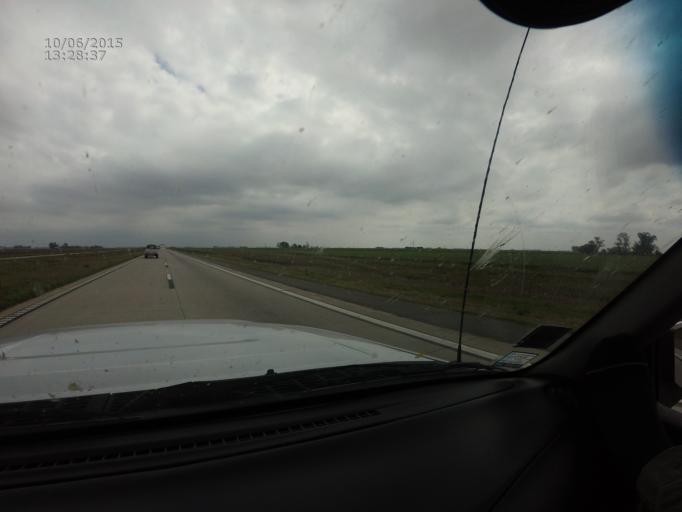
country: AR
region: Cordoba
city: Leones
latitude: -32.6414
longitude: -62.2272
